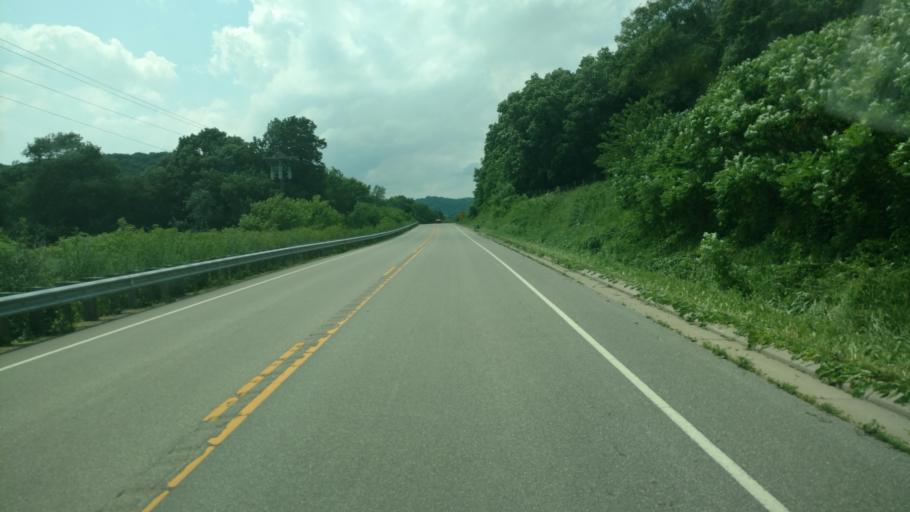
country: US
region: Wisconsin
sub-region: Vernon County
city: Viroqua
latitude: 43.4664
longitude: -90.7224
